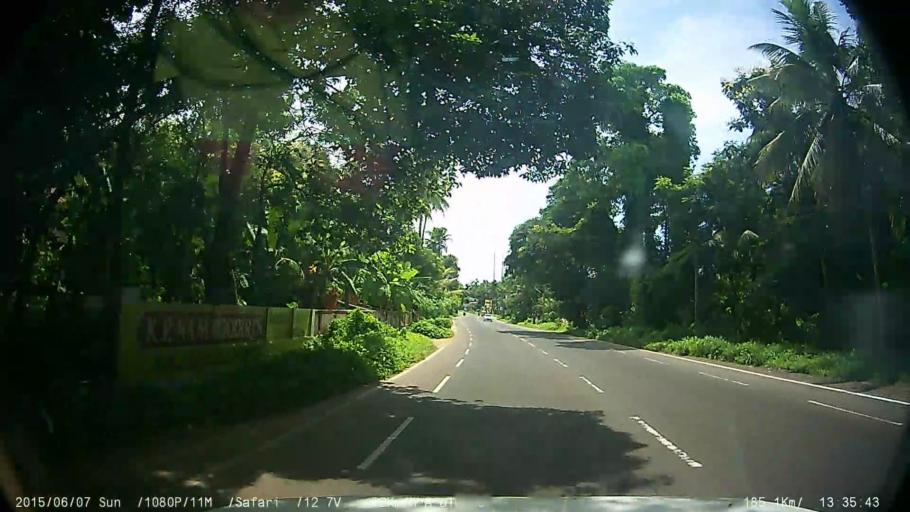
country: IN
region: Kerala
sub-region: Ernakulam
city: Perumbavoor
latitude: 10.0700
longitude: 76.5140
